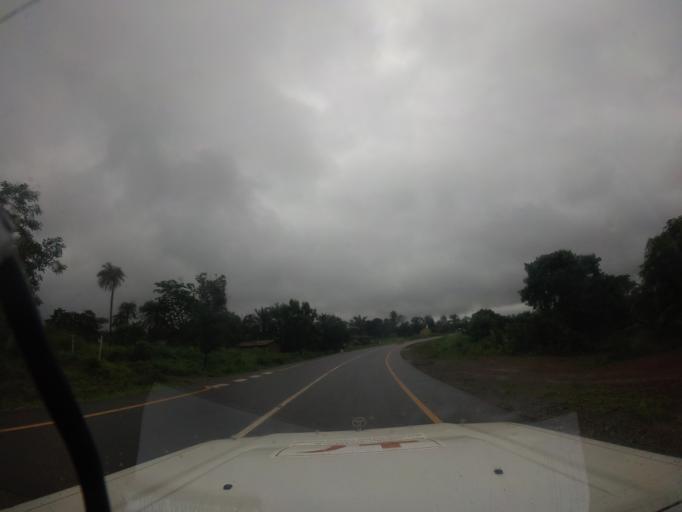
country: SL
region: Eastern Province
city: Hangha
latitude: 7.9361
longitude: -11.1465
